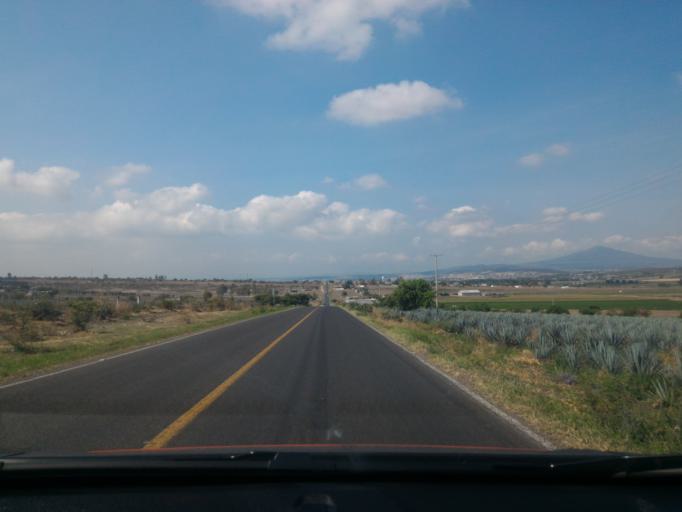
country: MX
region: Guanajuato
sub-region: Penjamo
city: Estacion la Piedad
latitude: 20.4238
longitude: -101.9928
